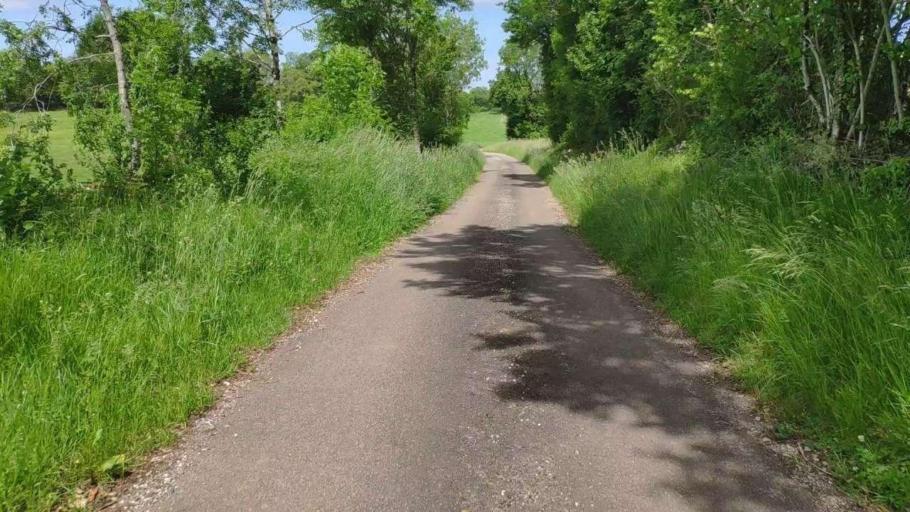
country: FR
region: Franche-Comte
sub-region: Departement du Jura
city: Perrigny
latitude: 46.7485
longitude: 5.6387
